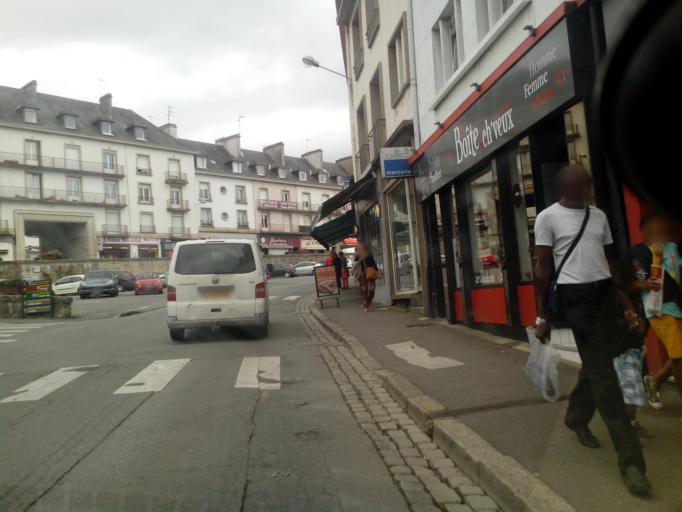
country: FR
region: Brittany
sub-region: Departement du Morbihan
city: Hennebont
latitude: 47.8053
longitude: -3.2783
